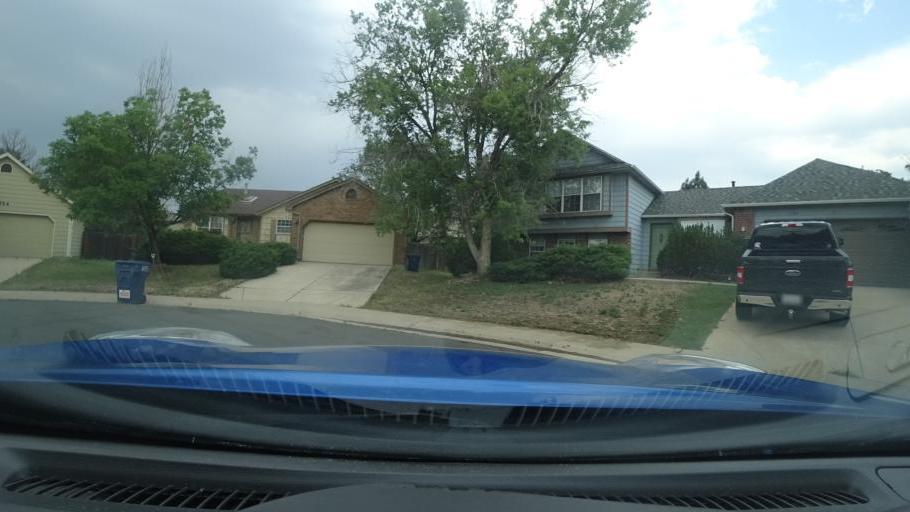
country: US
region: Colorado
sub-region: Adams County
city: Aurora
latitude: 39.6848
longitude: -104.7619
